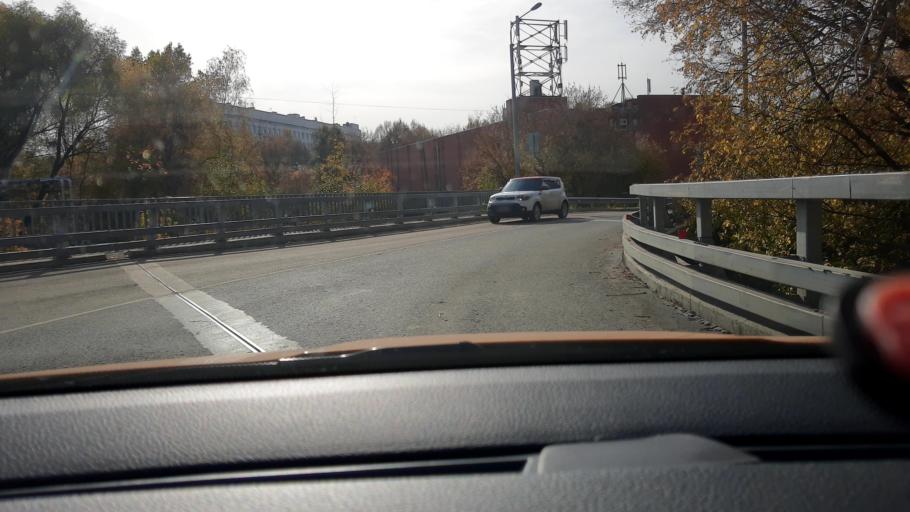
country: RU
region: Moscow
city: Babushkin
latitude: 55.8767
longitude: 37.7285
